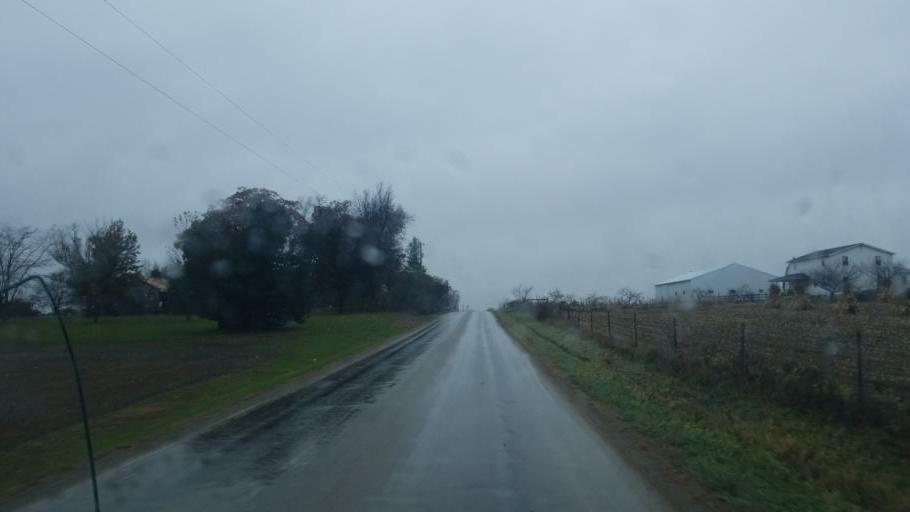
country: US
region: Indiana
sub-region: Adams County
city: Berne
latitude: 40.6248
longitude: -84.9356
